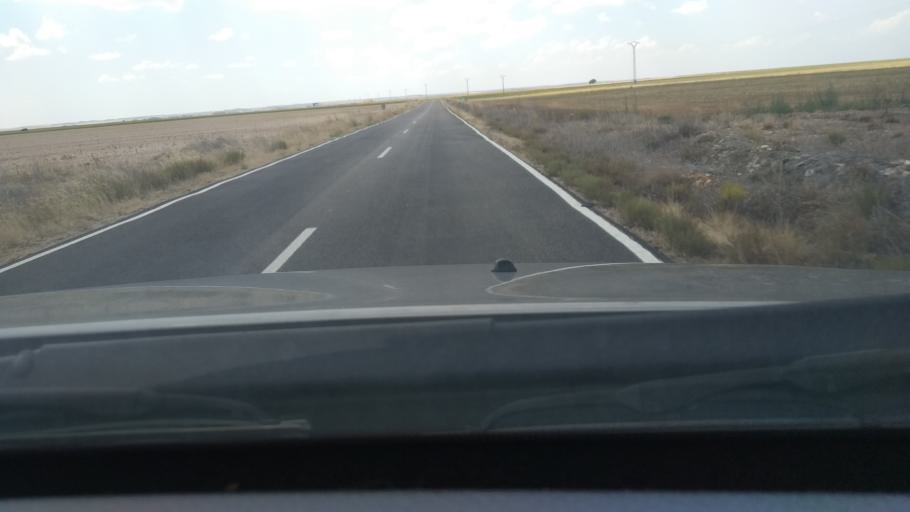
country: ES
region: Castille and Leon
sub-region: Provincia de Burgos
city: Iglesiarrubia
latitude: 41.9422
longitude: -3.8658
